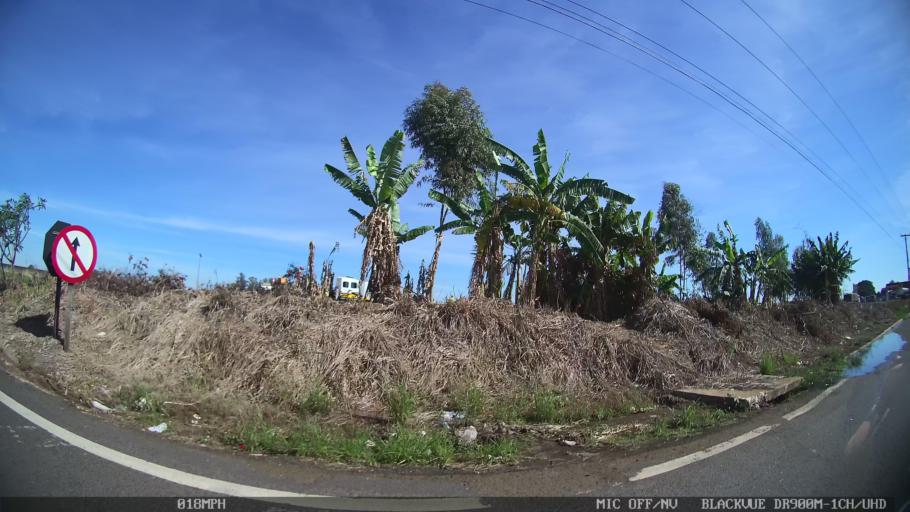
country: BR
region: Sao Paulo
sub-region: Pirassununga
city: Pirassununga
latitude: -22.0812
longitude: -47.4210
